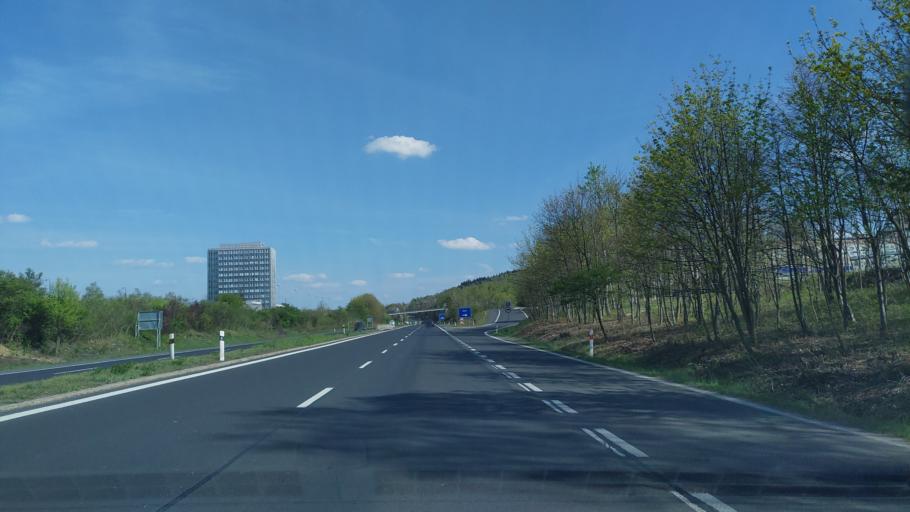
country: CZ
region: Ustecky
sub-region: Okres Most
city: Most
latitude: 50.5125
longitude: 13.6522
